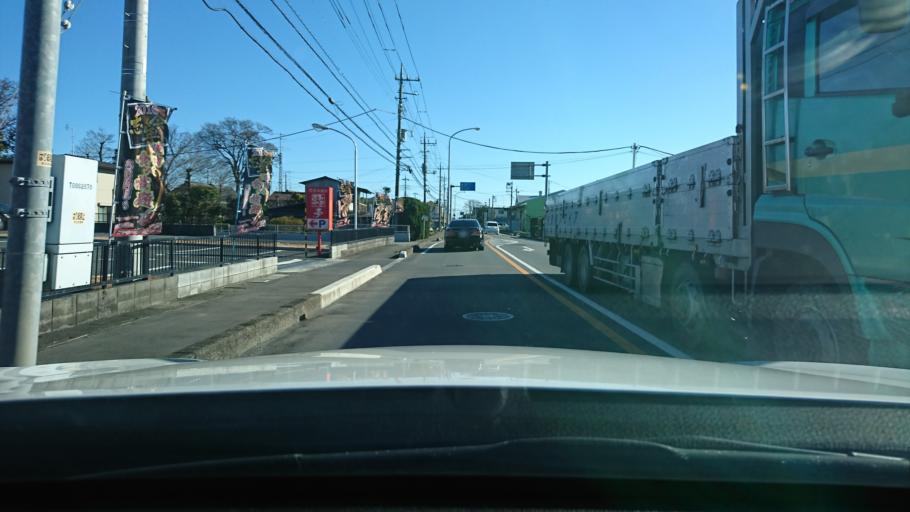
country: JP
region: Saitama
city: Kamifukuoka
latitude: 35.8825
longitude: 139.5342
